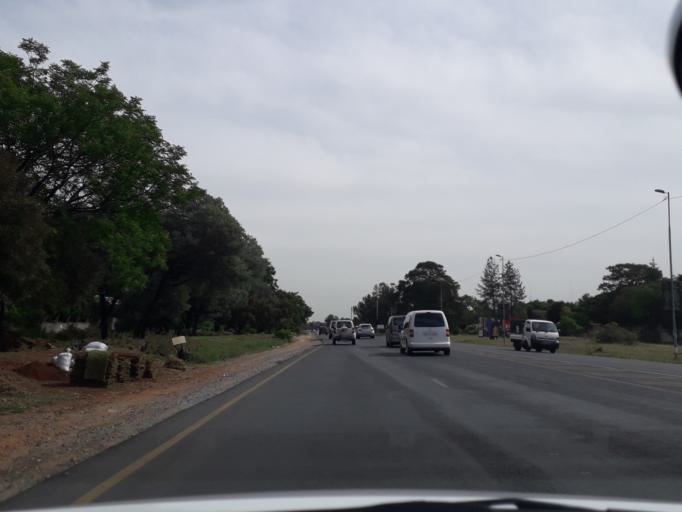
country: ZA
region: Gauteng
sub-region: City of Johannesburg Metropolitan Municipality
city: Diepsloot
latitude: -26.0186
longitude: 28.0335
